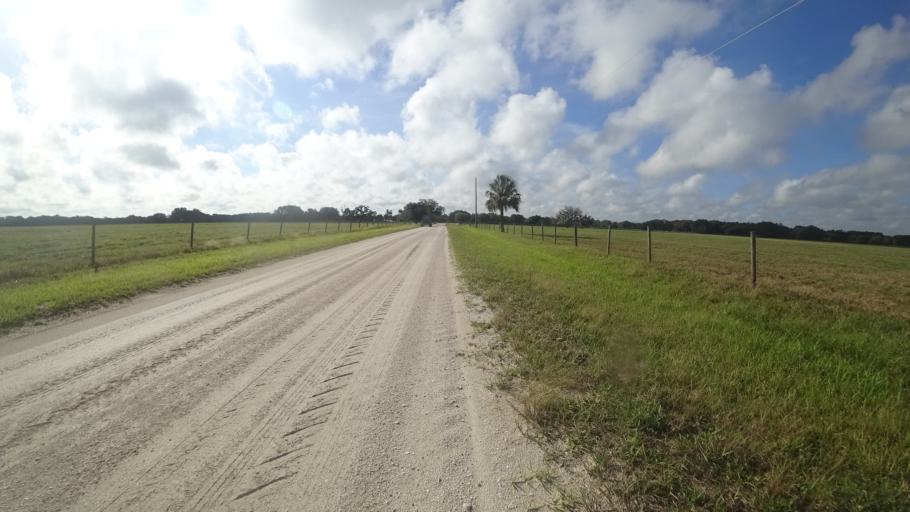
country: US
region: Florida
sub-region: Hillsborough County
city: Wimauma
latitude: 27.4705
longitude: -82.2273
